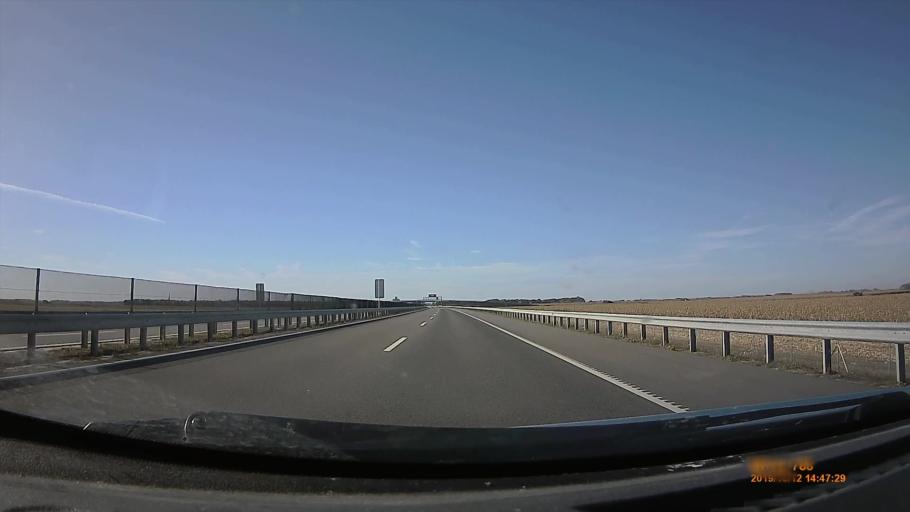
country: HU
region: Hajdu-Bihar
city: Berettyoujfalu
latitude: 47.2827
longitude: 21.5351
